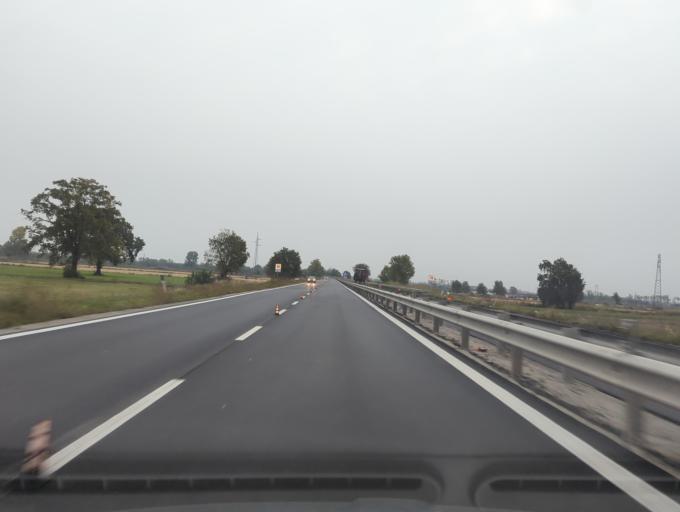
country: IT
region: Piedmont
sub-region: Provincia di Novara
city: Pernate
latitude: 45.4297
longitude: 8.6605
